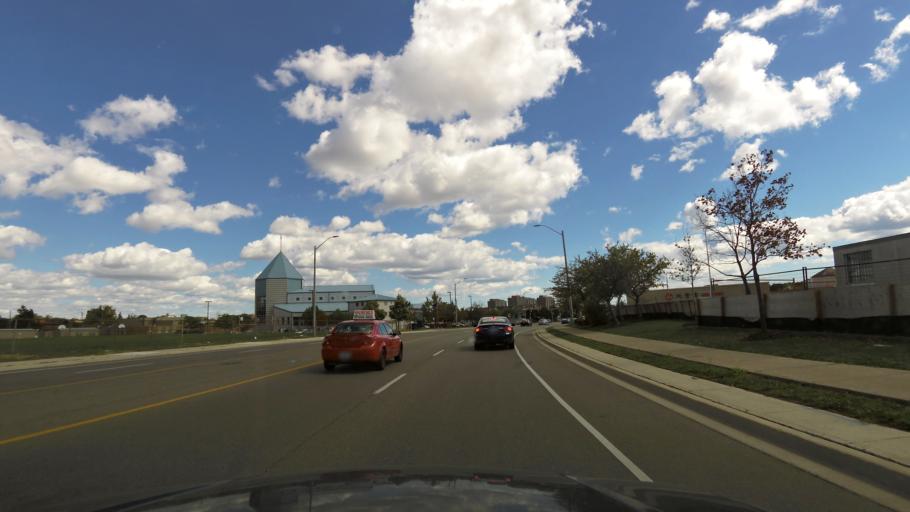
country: CA
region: Ontario
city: Mississauga
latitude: 43.5841
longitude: -79.6382
